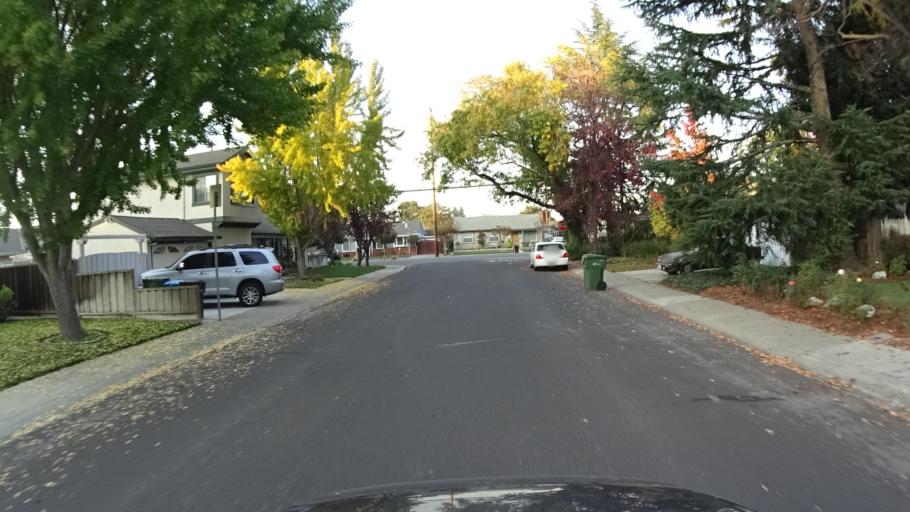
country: US
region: California
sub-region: Santa Clara County
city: Santa Clara
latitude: 37.3458
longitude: -121.9620
